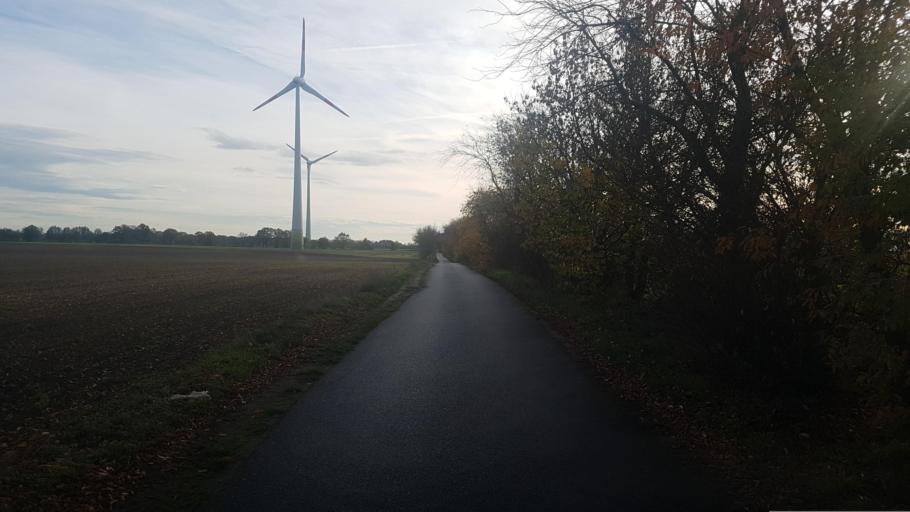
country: DE
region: Saxony-Anhalt
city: Abtsdorf
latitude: 51.8741
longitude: 12.7364
